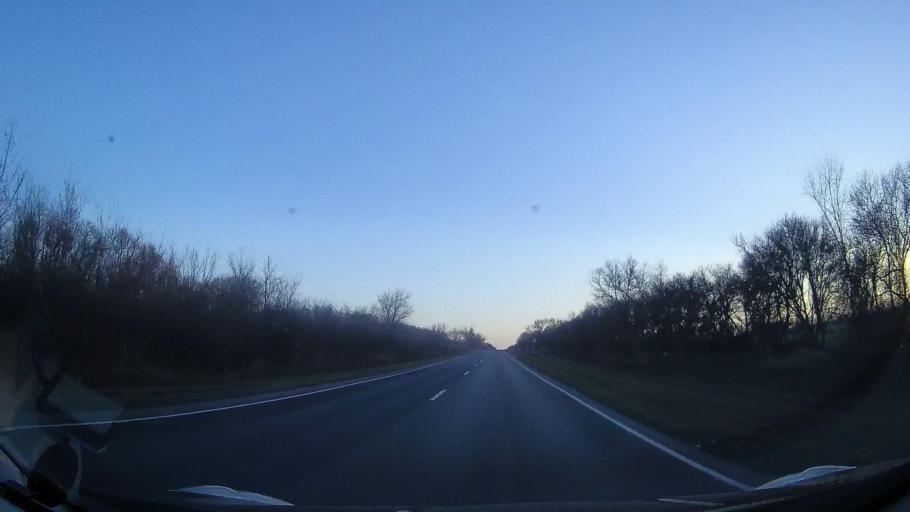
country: RU
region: Rostov
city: Bagayevskaya
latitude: 47.1370
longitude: 40.2766
